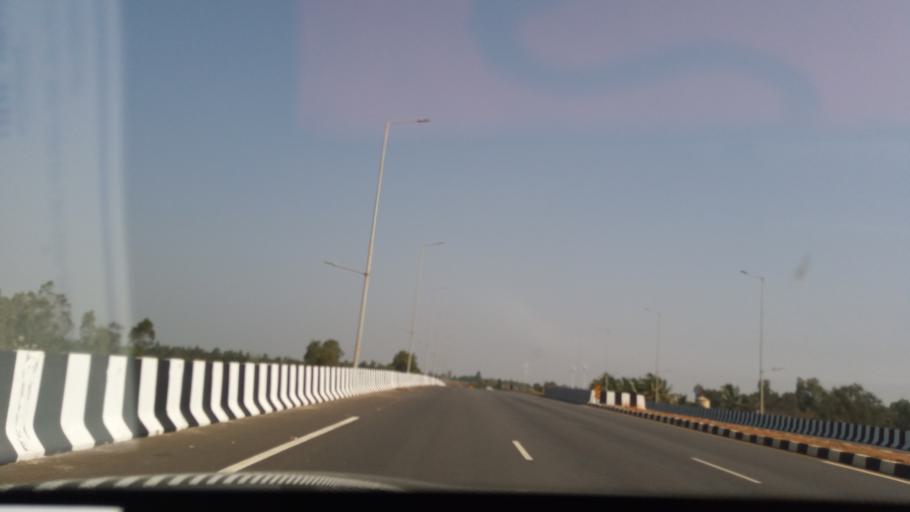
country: IN
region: Karnataka
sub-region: Haveri
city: Shiggaon
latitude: 15.1008
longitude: 75.1529
